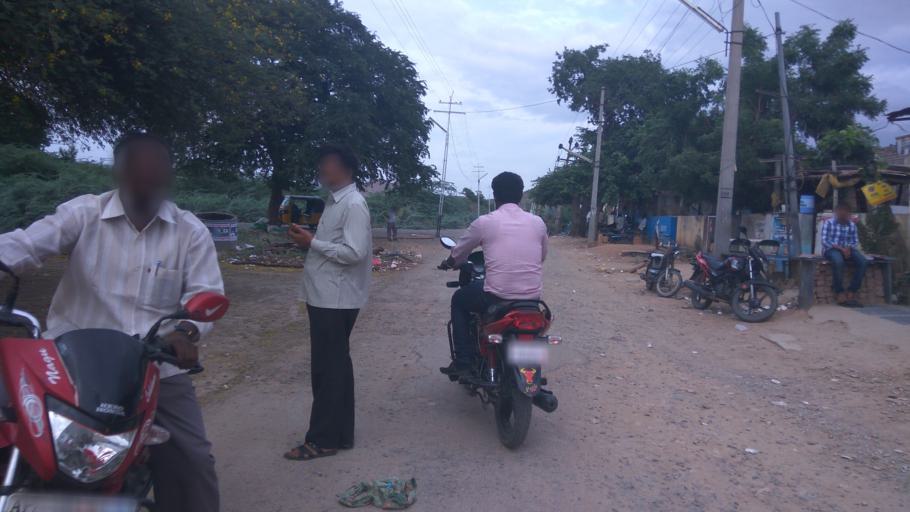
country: IN
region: Andhra Pradesh
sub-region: Prakasam
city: Cumbum
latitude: 15.5921
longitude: 79.1132
